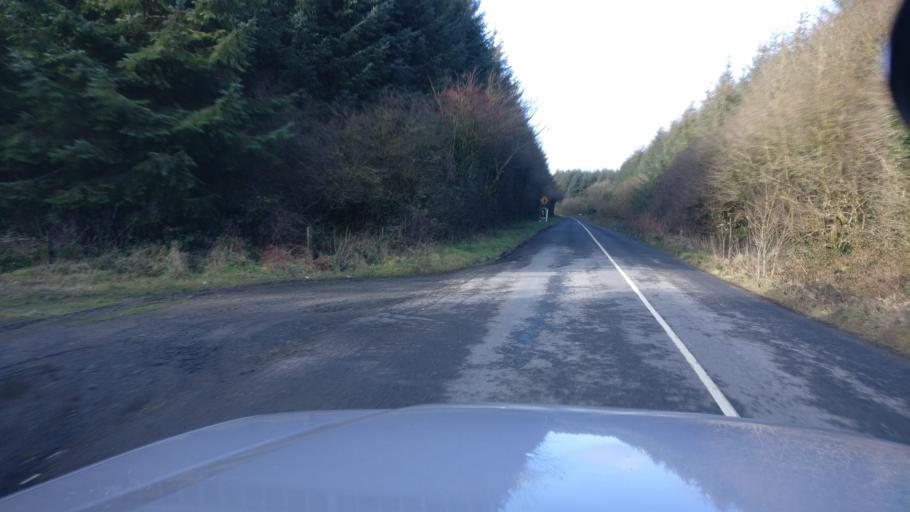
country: IE
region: Leinster
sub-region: Laois
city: Stradbally
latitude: 52.9131
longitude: -7.1831
